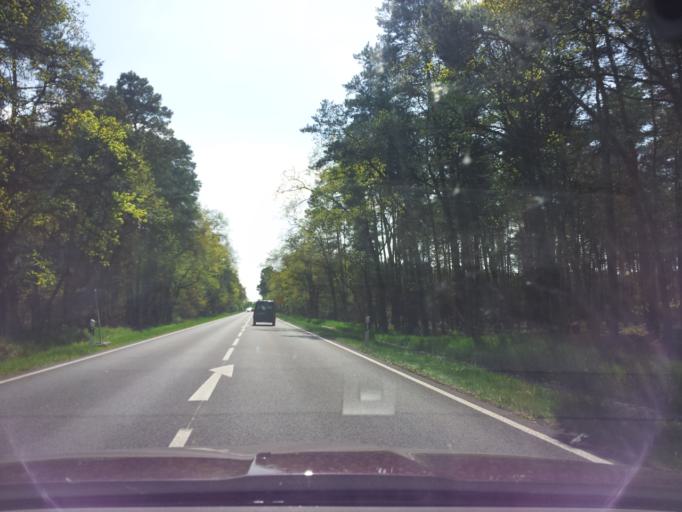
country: DE
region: Brandenburg
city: Treuenbrietzen
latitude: 52.1394
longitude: 12.9142
